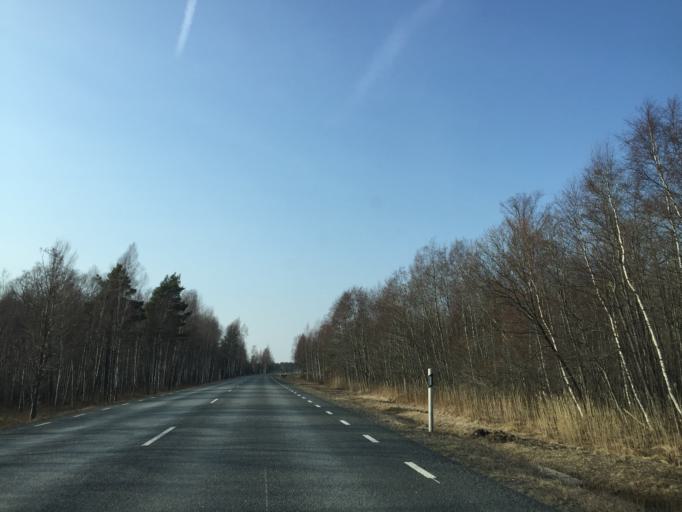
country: EE
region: Saare
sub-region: Orissaare vald
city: Orissaare
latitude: 58.5815
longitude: 23.3561
